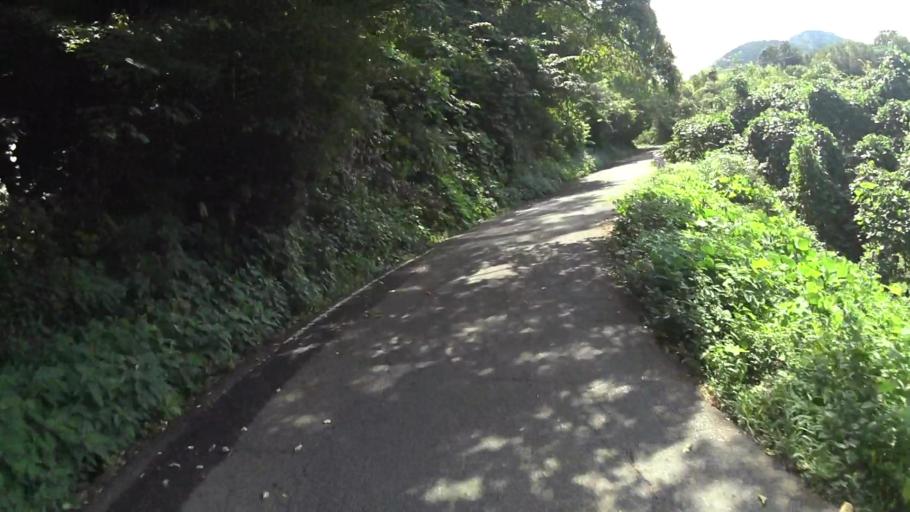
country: JP
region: Kyoto
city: Miyazu
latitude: 35.6761
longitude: 135.2390
